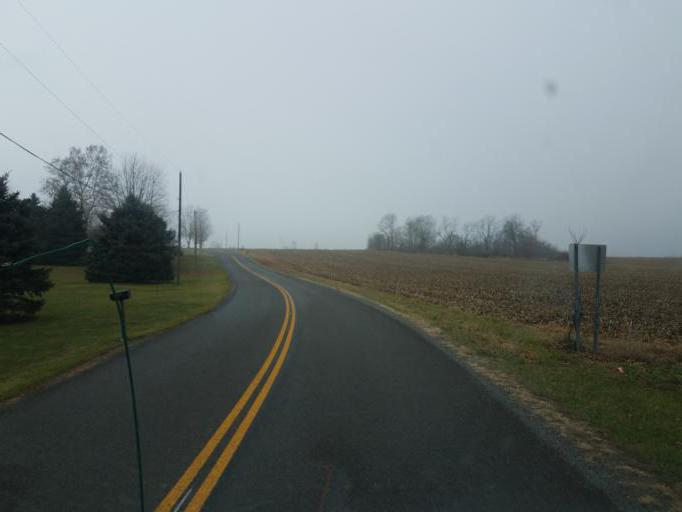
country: US
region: Ohio
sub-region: Champaign County
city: North Lewisburg
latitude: 40.2948
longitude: -83.5846
